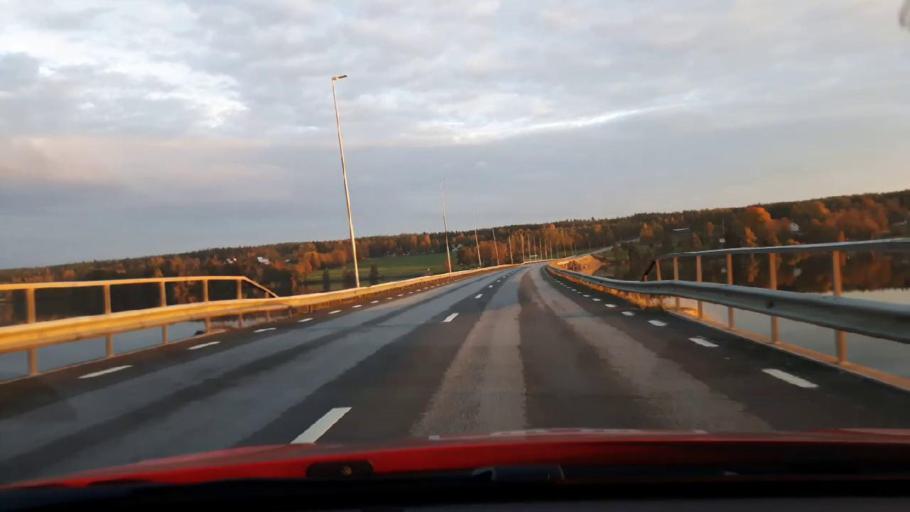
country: SE
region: Jaemtland
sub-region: OEstersunds Kommun
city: Lit
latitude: 63.3150
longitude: 14.8676
